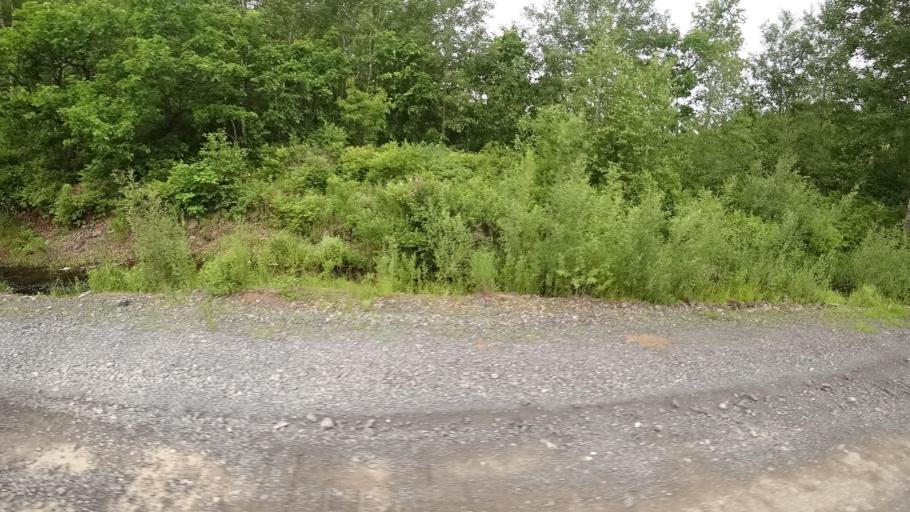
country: RU
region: Khabarovsk Krai
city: Amursk
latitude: 49.8951
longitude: 136.1220
